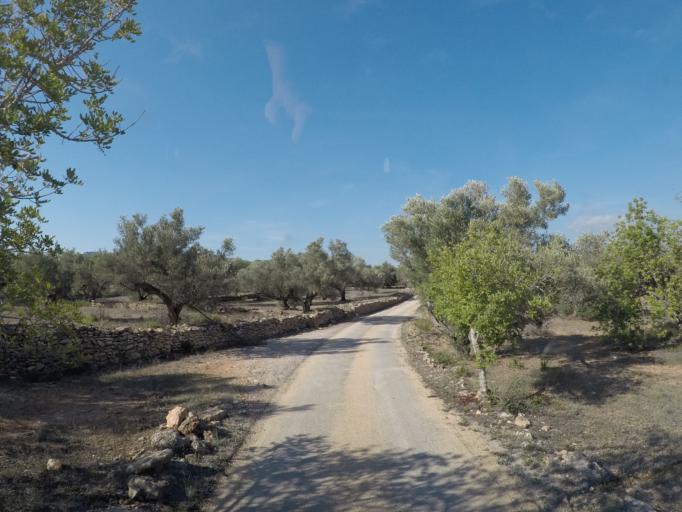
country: ES
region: Catalonia
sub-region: Provincia de Tarragona
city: El Perello
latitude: 40.9070
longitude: 0.7269
